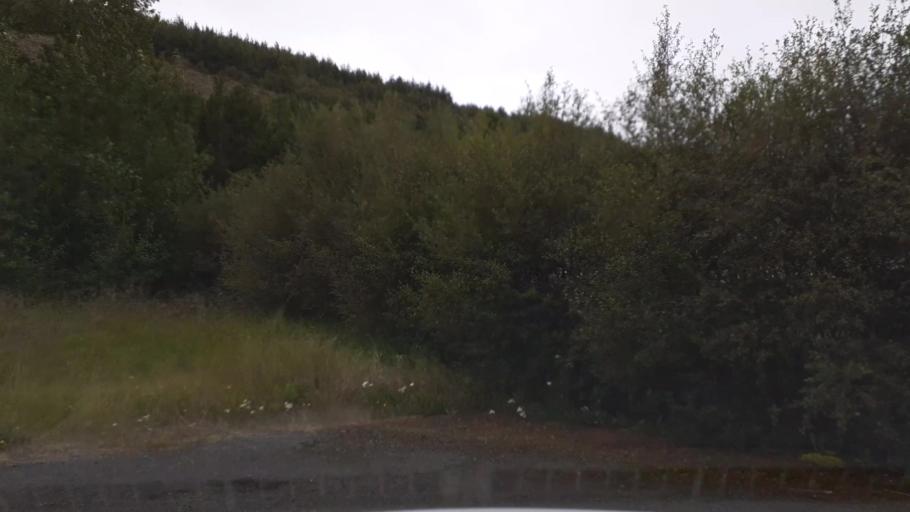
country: IS
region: Northwest
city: Saudarkrokur
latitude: 65.5552
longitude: -19.4519
